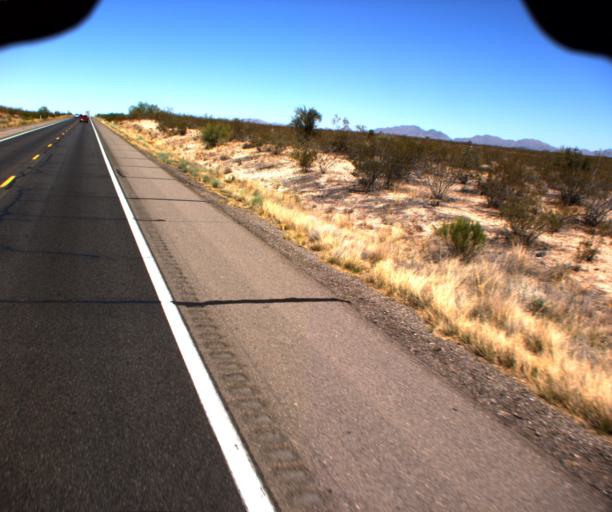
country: US
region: Arizona
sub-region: Yavapai County
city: Congress
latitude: 34.0456
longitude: -112.8387
